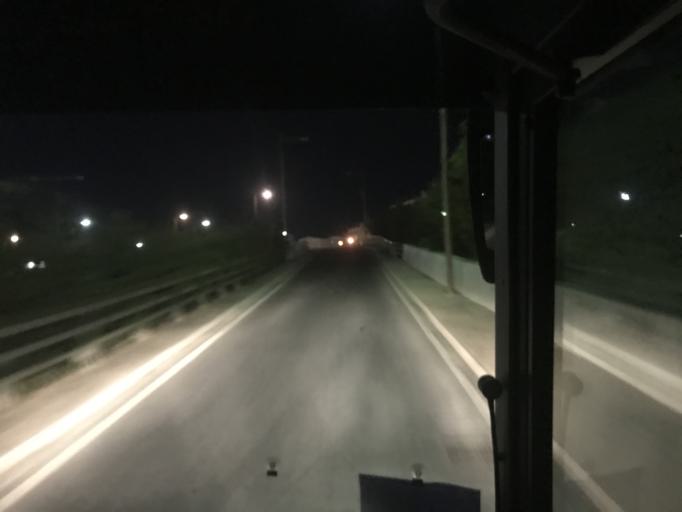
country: GR
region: Crete
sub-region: Nomos Irakleiou
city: Irakleion
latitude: 35.3254
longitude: 25.1396
